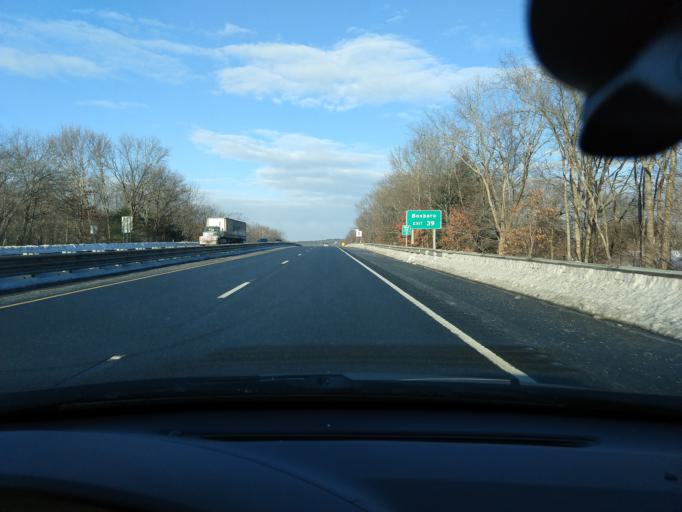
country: US
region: Massachusetts
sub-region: Middlesex County
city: Littleton Common
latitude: 42.5169
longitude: -71.4995
